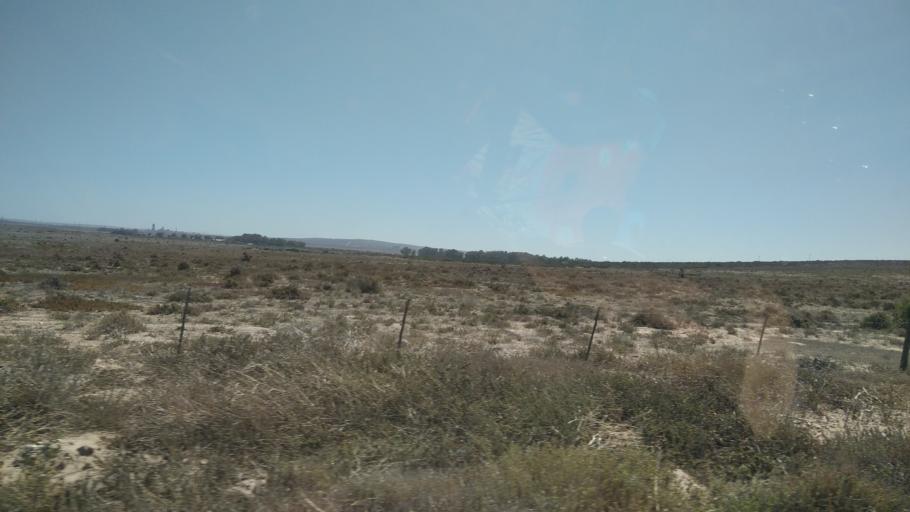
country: ZA
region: Western Cape
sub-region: West Coast District Municipality
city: Vredenburg
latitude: -33.0149
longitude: 18.1146
